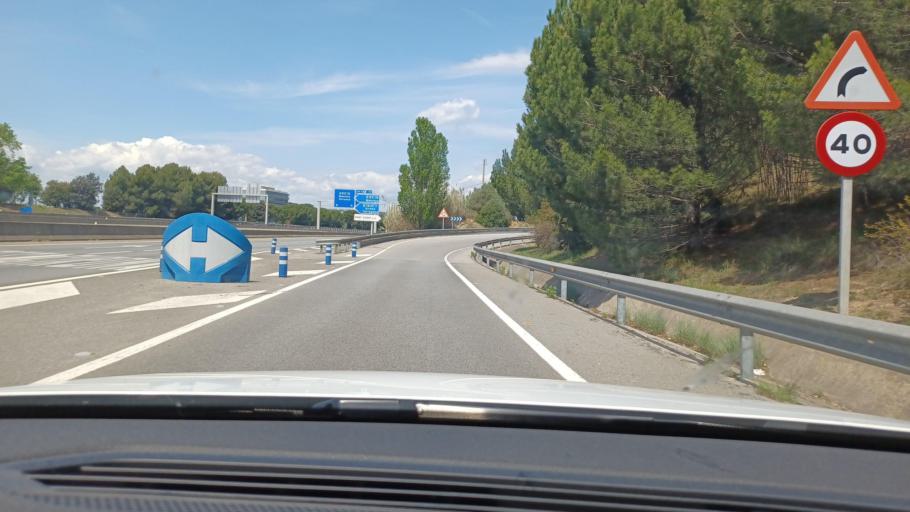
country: ES
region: Catalonia
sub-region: Provincia de Barcelona
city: Sant Cugat del Valles
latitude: 41.4837
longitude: 2.0632
